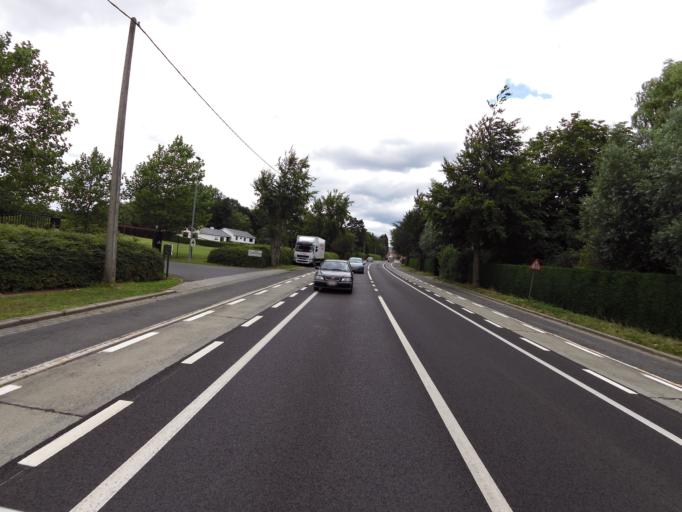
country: BE
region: Flanders
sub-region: Provincie West-Vlaanderen
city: Hooglede
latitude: 50.9710
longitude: 3.0871
